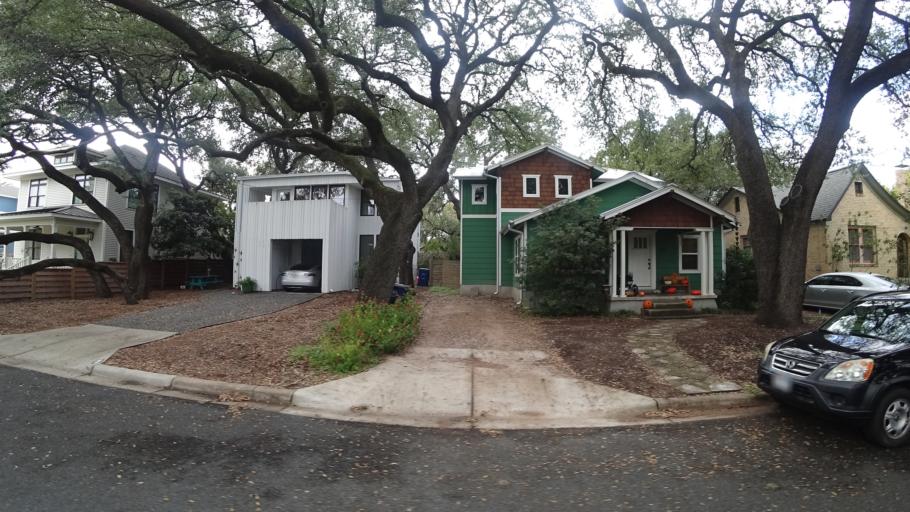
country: US
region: Texas
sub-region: Travis County
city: Austin
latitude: 30.2550
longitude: -97.7572
